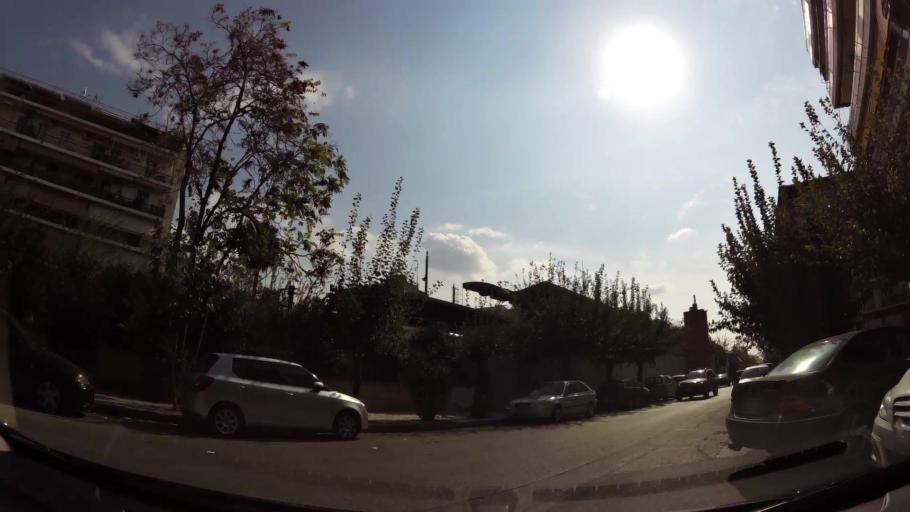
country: GR
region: Attica
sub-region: Nomarchia Athinas
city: Nea Chalkidona
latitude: 38.0206
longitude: 23.7317
